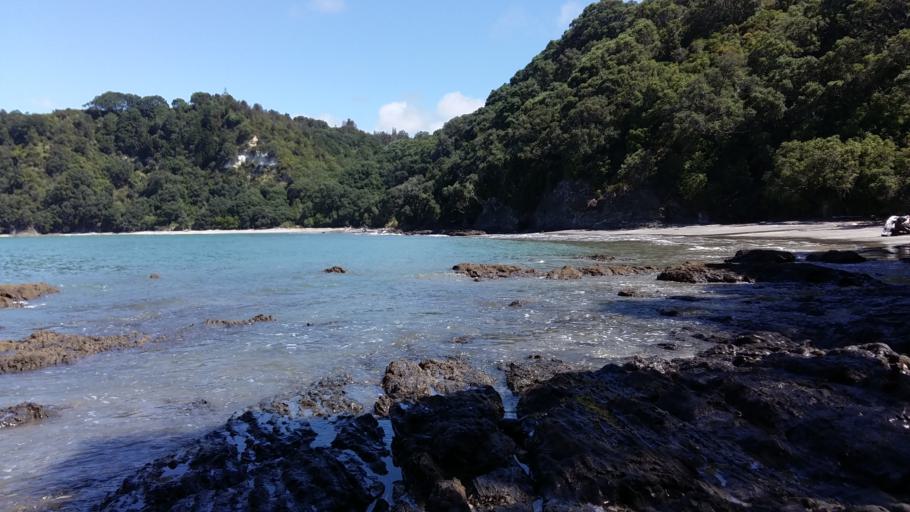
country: NZ
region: Bay of Plenty
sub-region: Whakatane District
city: Whakatane
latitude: -37.9468
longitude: 177.0208
